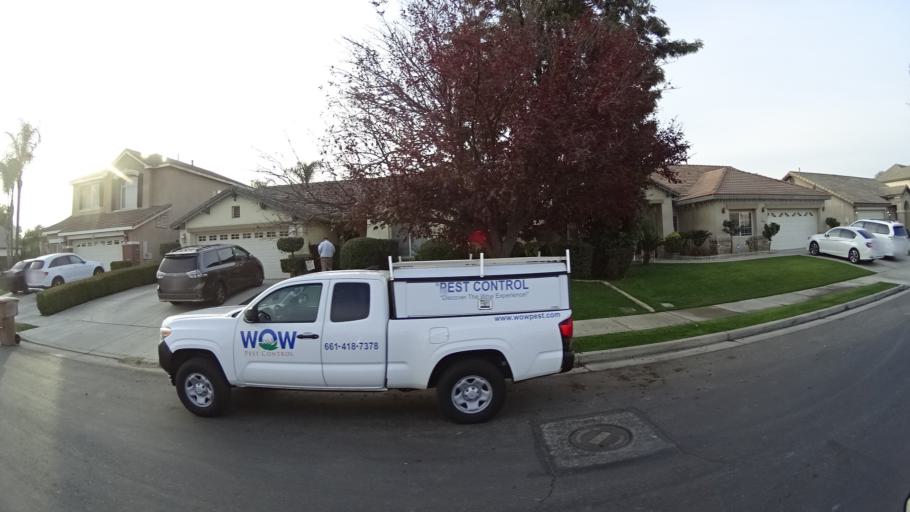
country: US
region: California
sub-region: Kern County
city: Greenacres
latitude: 35.4198
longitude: -119.1198
